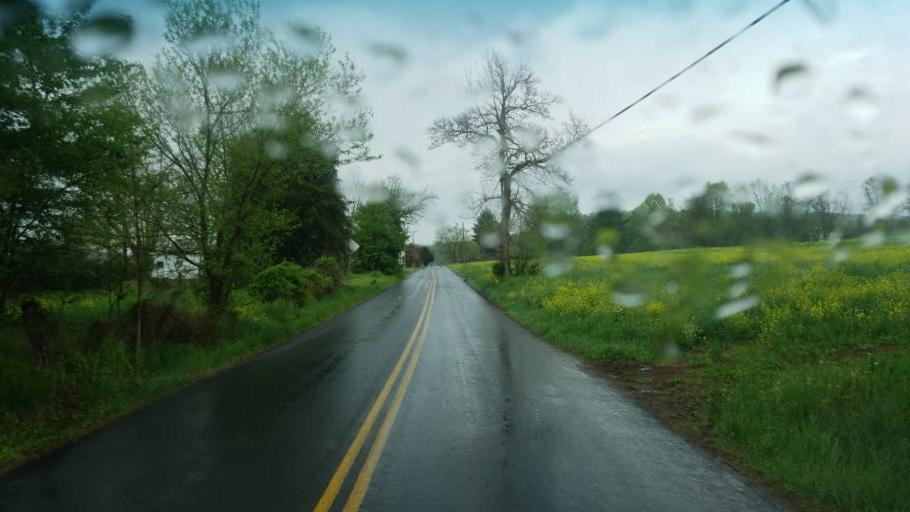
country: US
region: Virginia
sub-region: Smyth County
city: Adwolf
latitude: 36.7692
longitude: -81.5668
